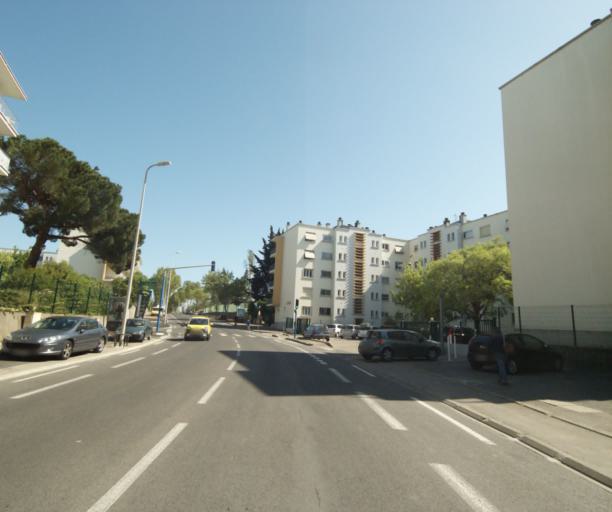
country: FR
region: Languedoc-Roussillon
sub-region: Departement de l'Herault
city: Montpellier
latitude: 43.6187
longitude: 3.8589
